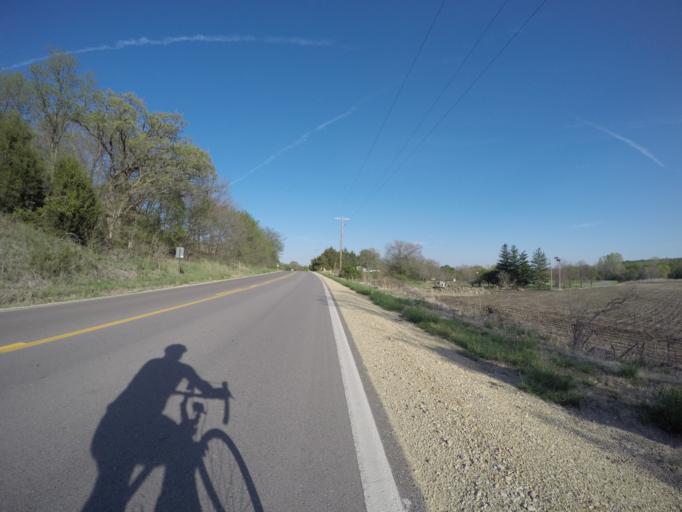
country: US
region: Kansas
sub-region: Riley County
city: Ogden
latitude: 39.2260
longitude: -96.7128
